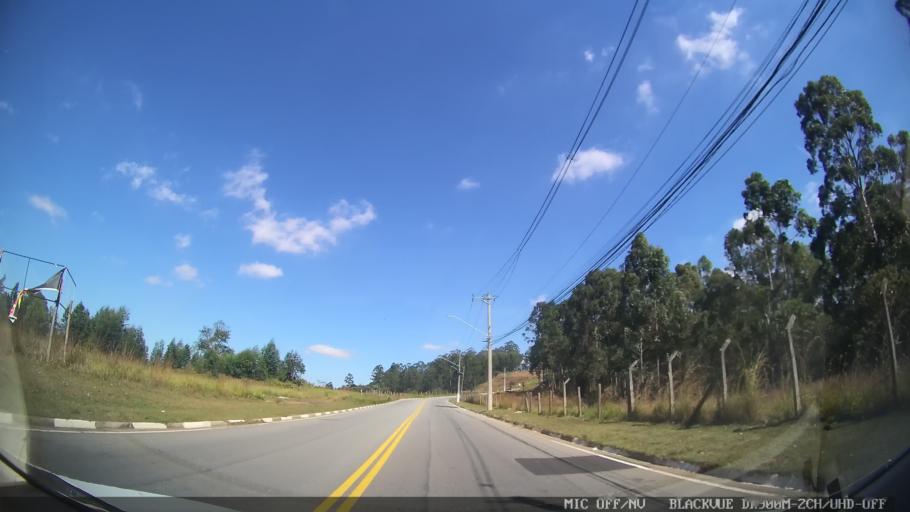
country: BR
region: Sao Paulo
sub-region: Barueri
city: Barueri
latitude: -23.4522
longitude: -46.8385
